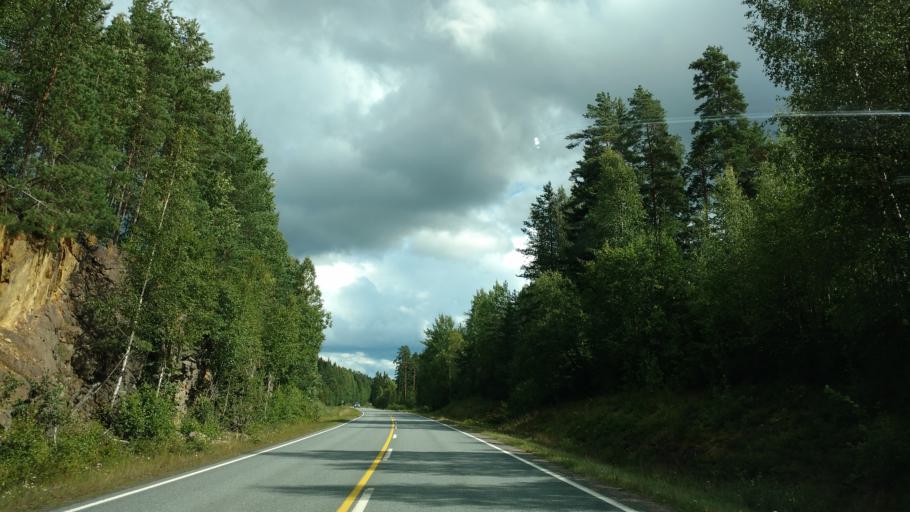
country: FI
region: Varsinais-Suomi
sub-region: Salo
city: Kisko
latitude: 60.2462
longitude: 23.5010
